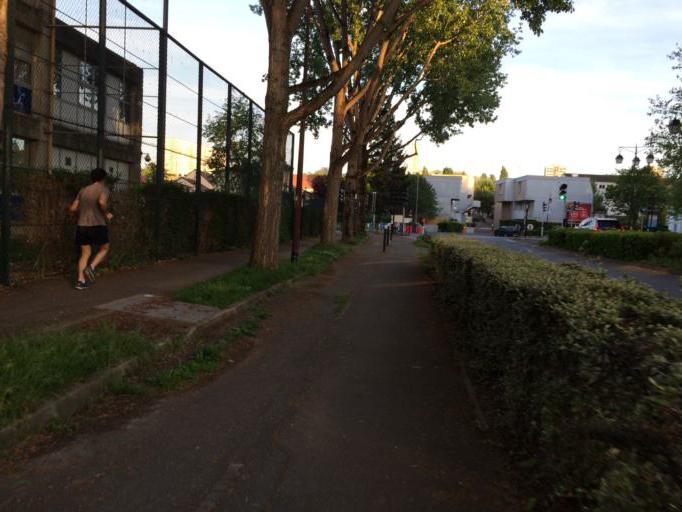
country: FR
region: Ile-de-France
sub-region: Departement de l'Essonne
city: Massy
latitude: 48.7427
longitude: 2.2852
